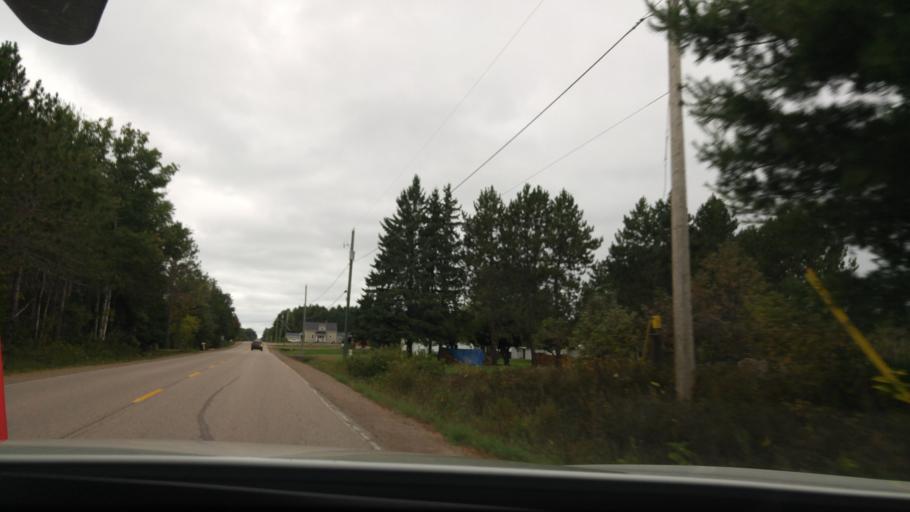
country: CA
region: Ontario
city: Petawawa
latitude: 45.8300
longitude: -77.2705
